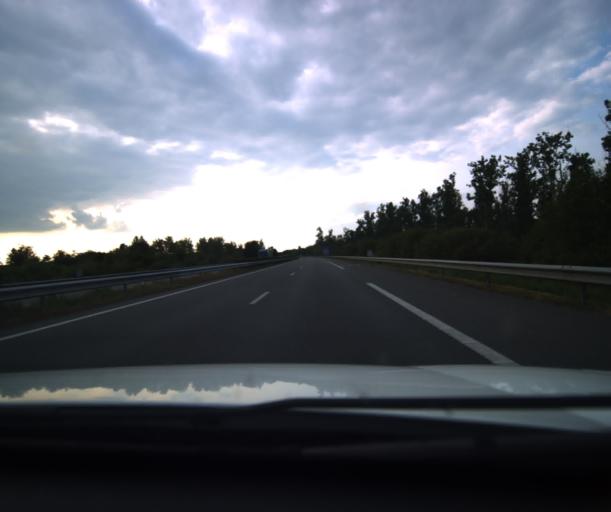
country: FR
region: Midi-Pyrenees
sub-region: Departement du Tarn-et-Garonne
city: Saint-Porquier
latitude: 44.0032
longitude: 1.2231
